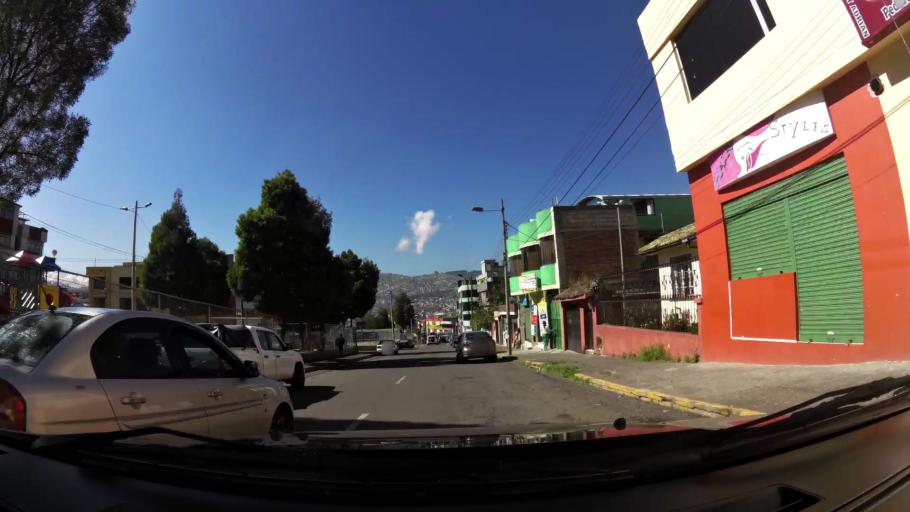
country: EC
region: Pichincha
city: Quito
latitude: -0.2367
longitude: -78.5300
